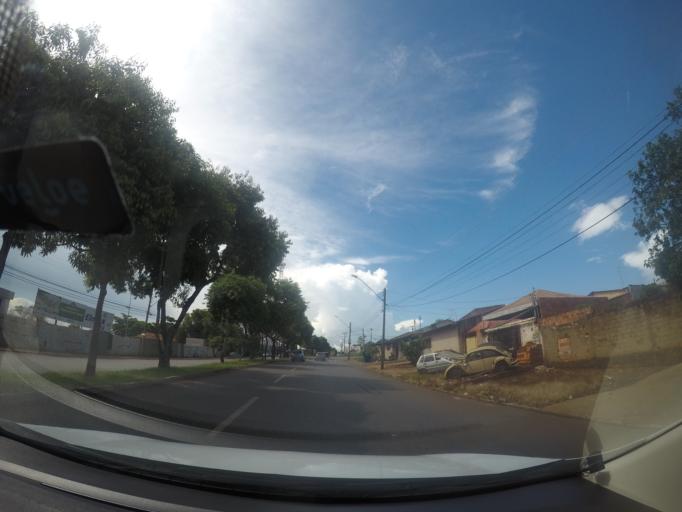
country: BR
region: Goias
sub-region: Trindade
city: Trindade
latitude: -16.6635
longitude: -49.3869
